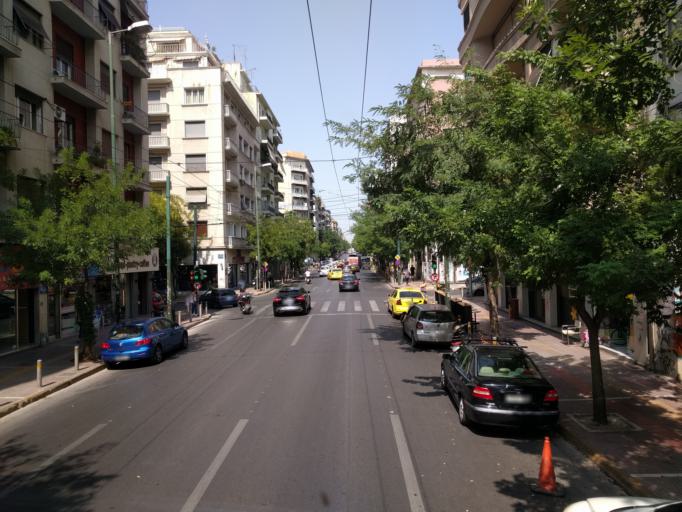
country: GR
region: Attica
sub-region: Nomarchia Athinas
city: Athens
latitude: 37.9875
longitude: 23.7288
